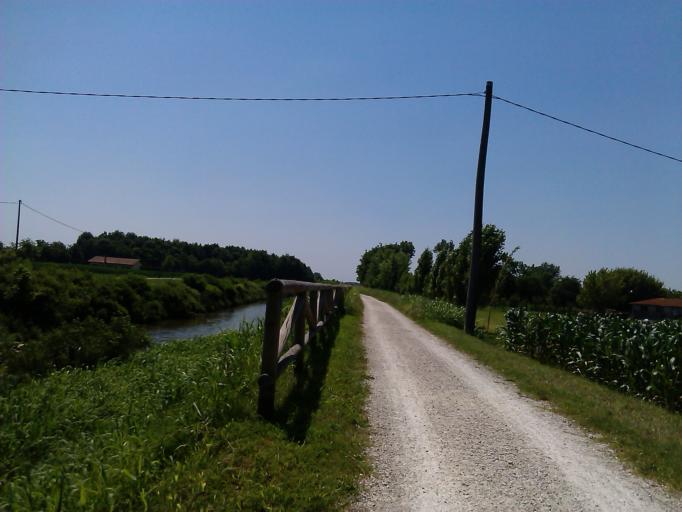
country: IT
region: Veneto
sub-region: Provincia di Padova
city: Loreggiola
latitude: 45.6247
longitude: 11.9263
